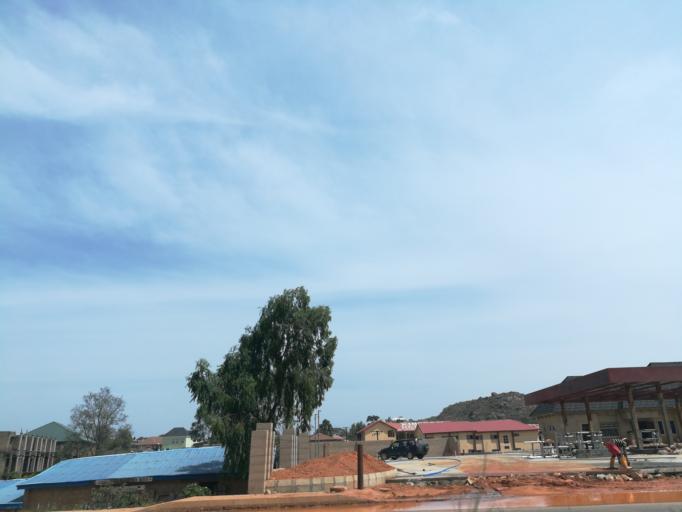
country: NG
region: Plateau
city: Bukuru
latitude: 9.8455
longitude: 8.8665
